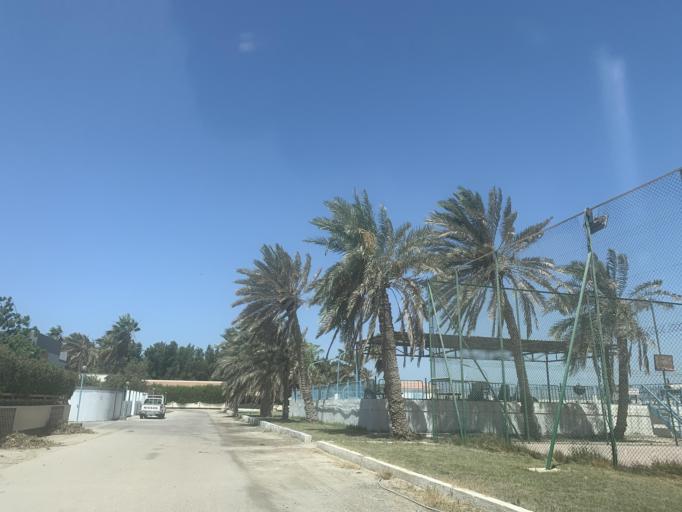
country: BH
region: Manama
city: Jidd Hafs
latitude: 26.2186
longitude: 50.4531
